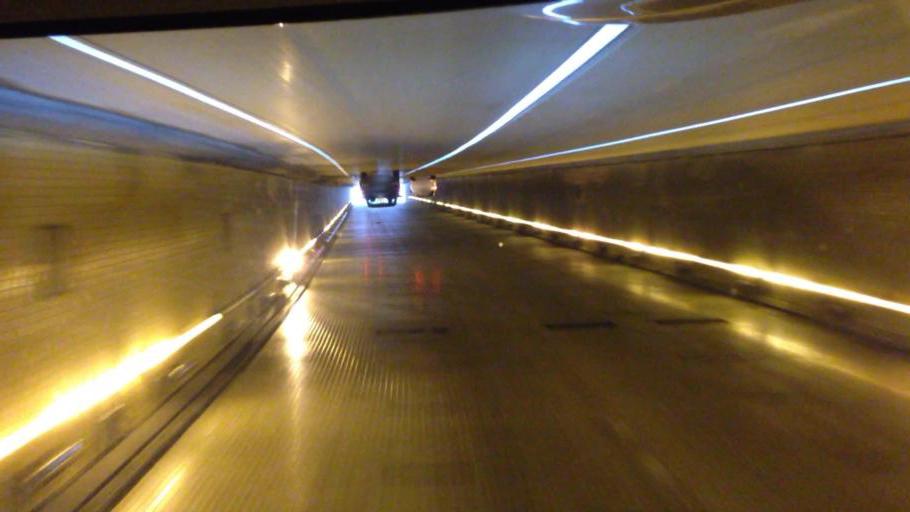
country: US
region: Minnesota
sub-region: Hennepin County
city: Minneapolis
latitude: 44.9667
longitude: -93.2878
